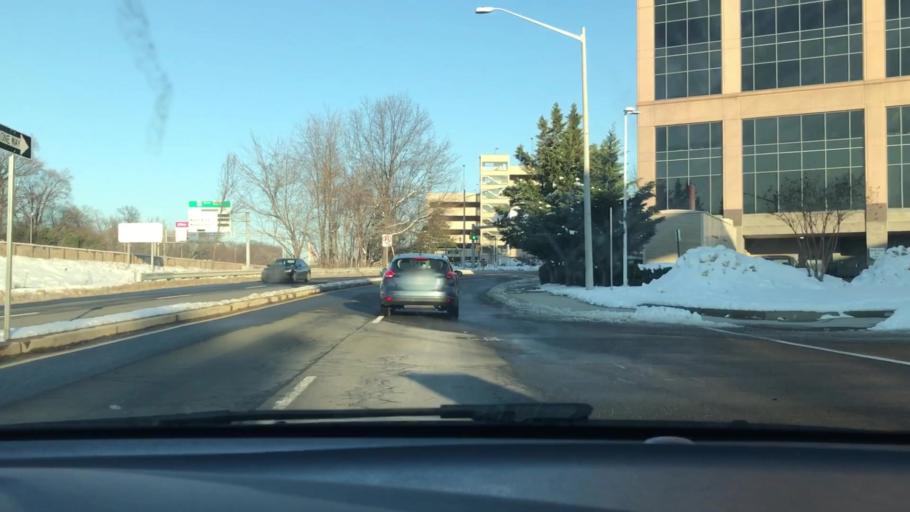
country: US
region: Virginia
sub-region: Fairfax County
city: Merrifield
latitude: 38.8808
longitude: -77.2342
